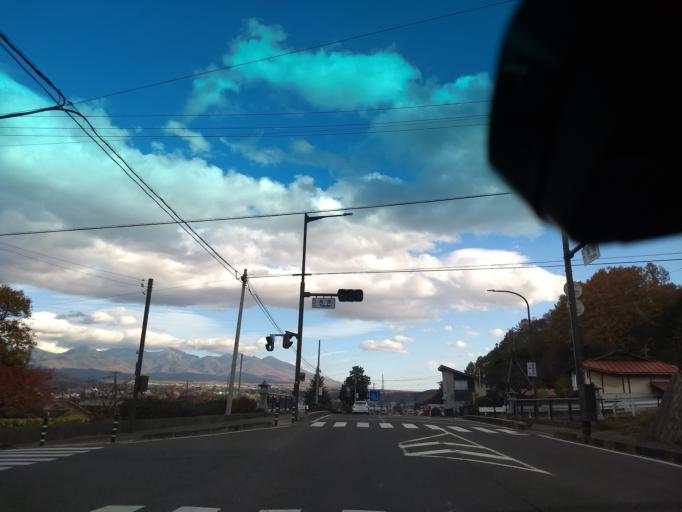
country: JP
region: Nagano
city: Chino
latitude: 35.9958
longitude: 138.1296
